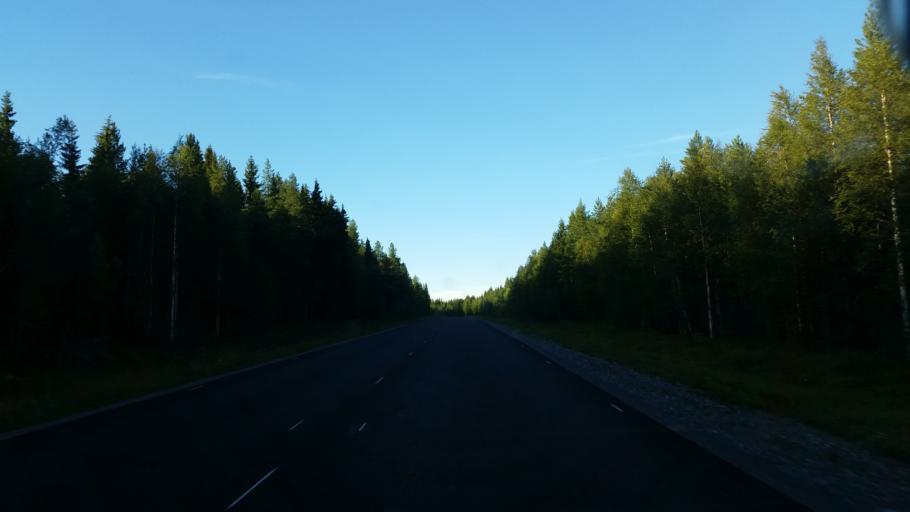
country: SE
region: Vaesterbotten
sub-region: Dorotea Kommun
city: Dorotea
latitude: 64.3070
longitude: 16.5971
